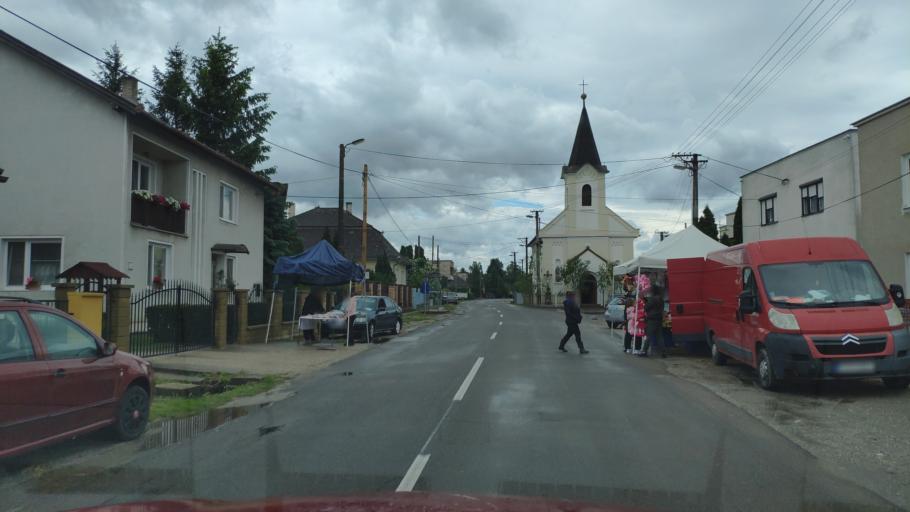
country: SK
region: Kosicky
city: Moldava nad Bodvou
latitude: 48.5738
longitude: 21.1211
